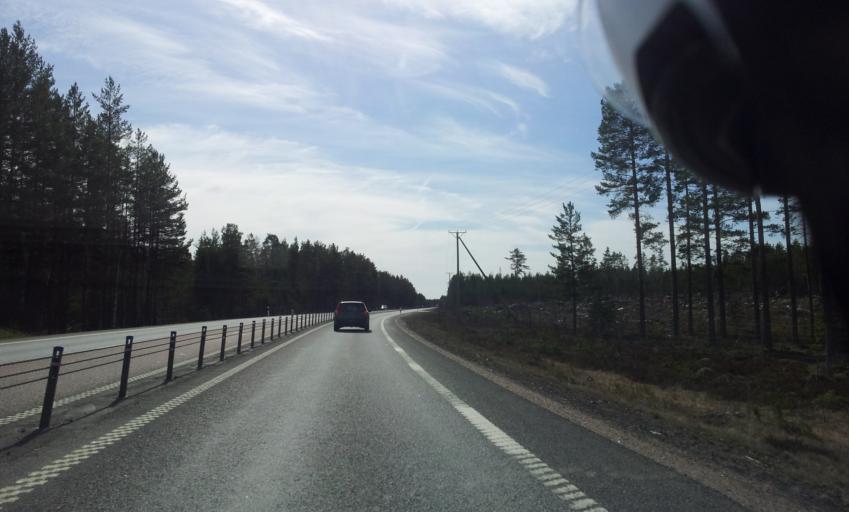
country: SE
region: Gaevleborg
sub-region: Gavle Kommun
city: Norrsundet
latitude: 61.0305
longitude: 16.9743
